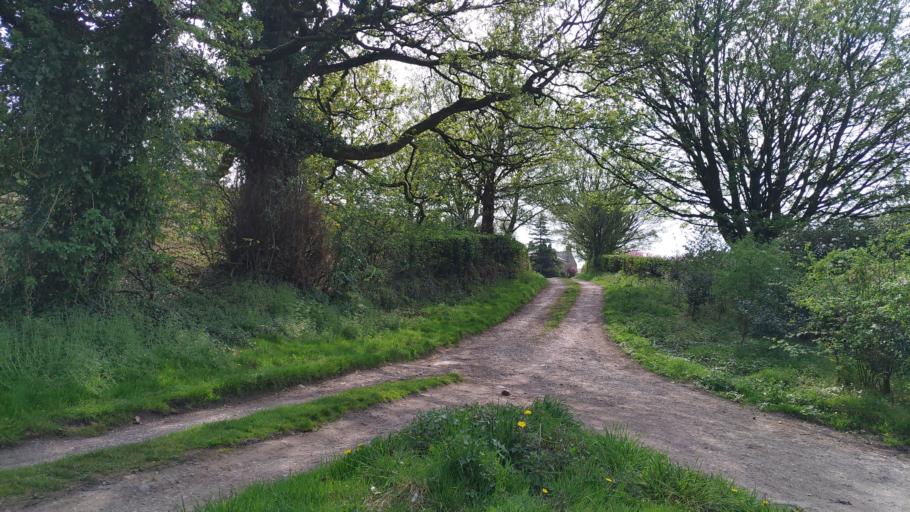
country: GB
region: England
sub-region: Lancashire
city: Chorley
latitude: 53.6668
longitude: -2.5799
